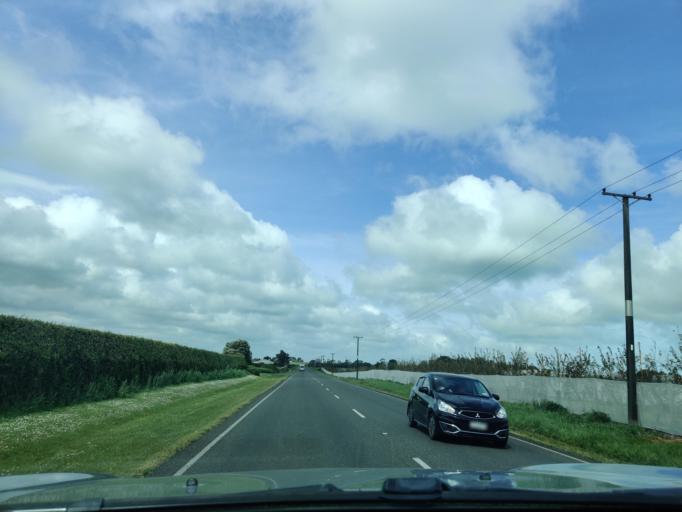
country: NZ
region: Taranaki
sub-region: South Taranaki District
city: Patea
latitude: -39.8091
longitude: 174.7692
